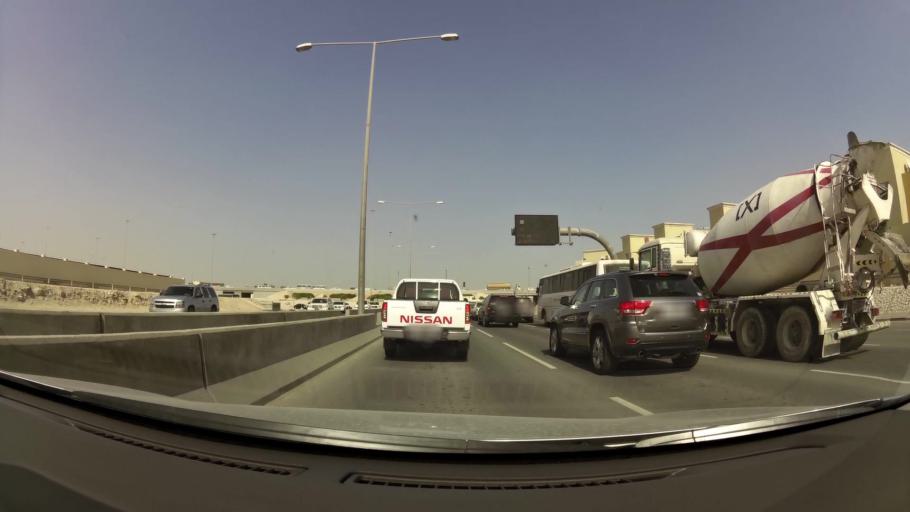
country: QA
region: Baladiyat ar Rayyan
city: Ar Rayyan
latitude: 25.3435
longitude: 51.4565
